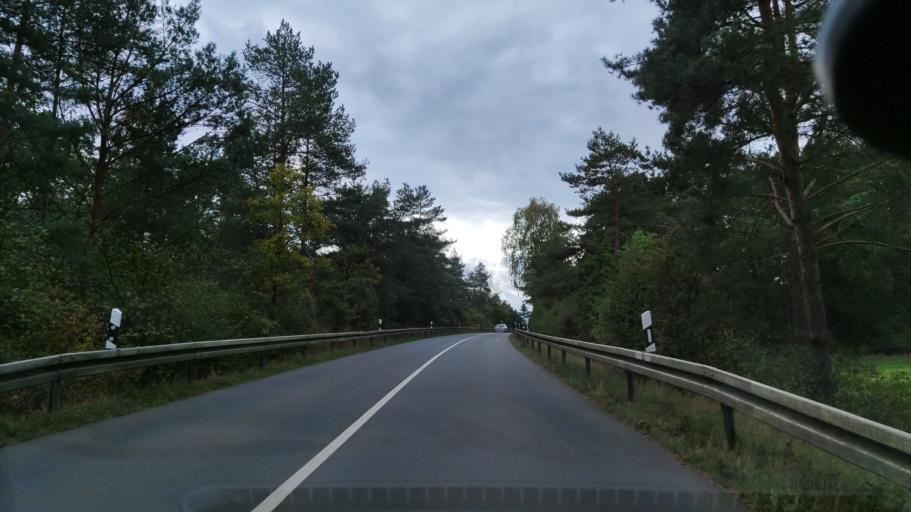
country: DE
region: Lower Saxony
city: Vastorf
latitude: 53.1738
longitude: 10.5200
